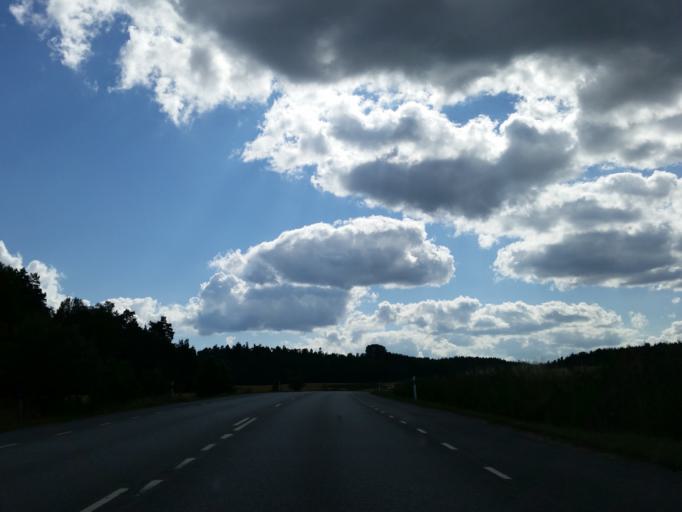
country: SE
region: Soedermanland
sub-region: Trosa Kommun
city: Vagnharad
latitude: 58.9512
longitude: 17.5476
